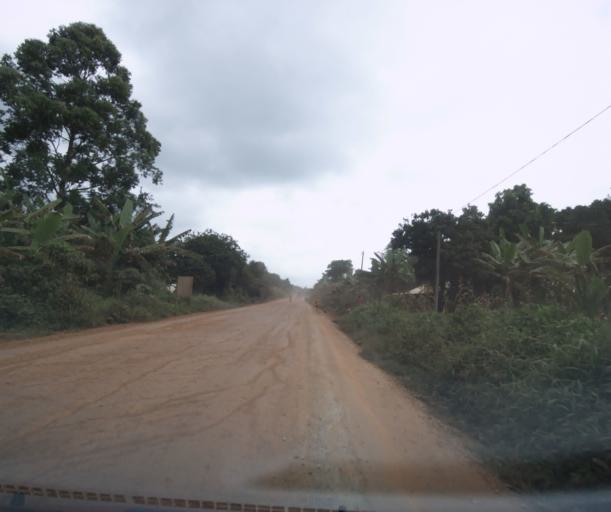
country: CM
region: West
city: Mbouda
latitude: 5.6694
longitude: 10.2176
